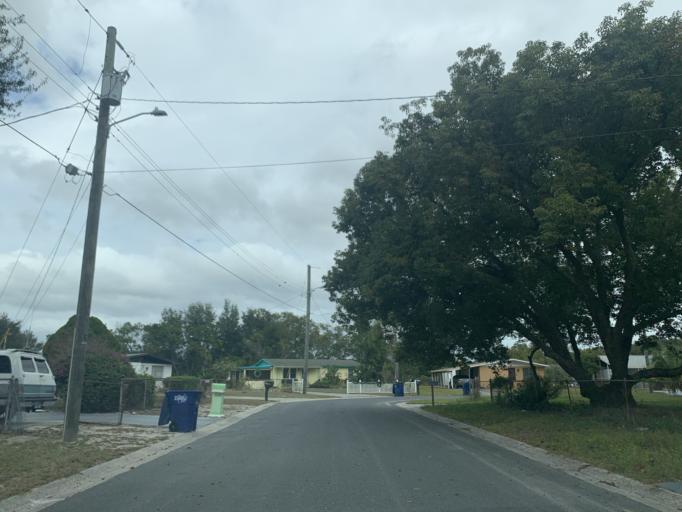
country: US
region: Florida
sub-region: Hillsborough County
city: East Lake-Orient Park
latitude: 27.9733
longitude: -82.4084
